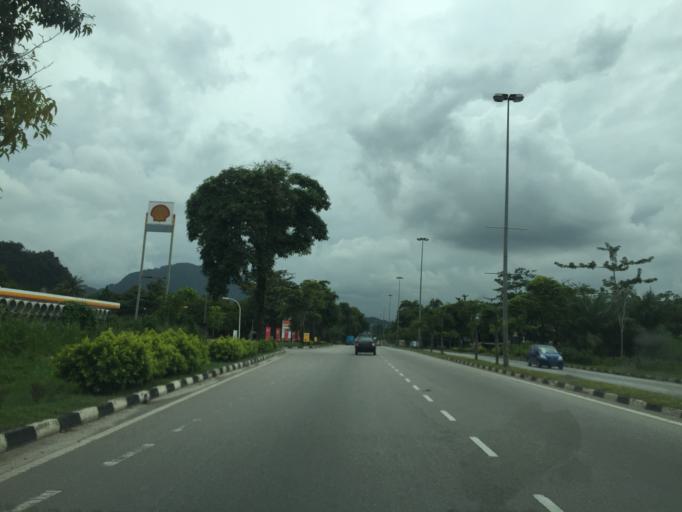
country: MY
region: Perak
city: Ipoh
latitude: 4.5436
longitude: 101.1207
